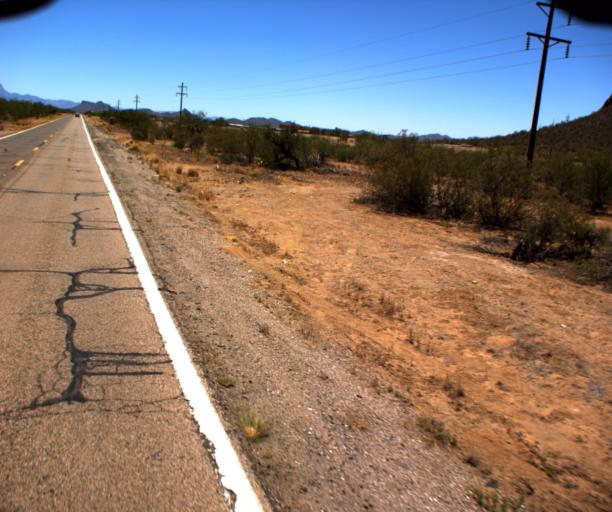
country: US
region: Arizona
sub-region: Pima County
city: Sells
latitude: 31.9536
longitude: -111.9415
